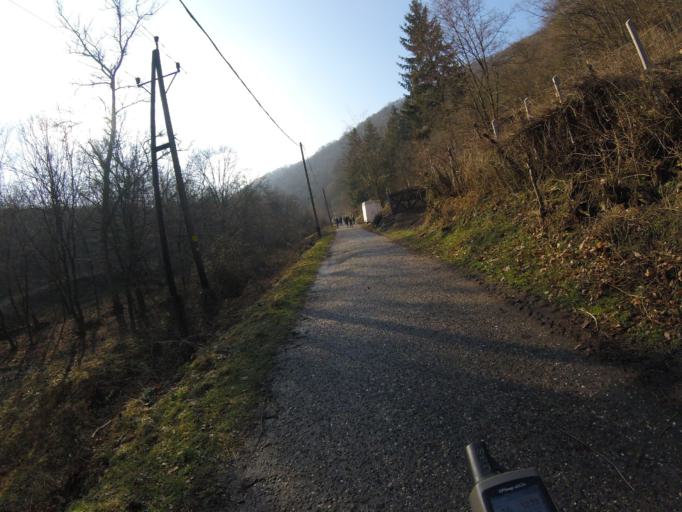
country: HU
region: Komarom-Esztergom
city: Pilismarot
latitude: 47.7541
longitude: 18.9059
